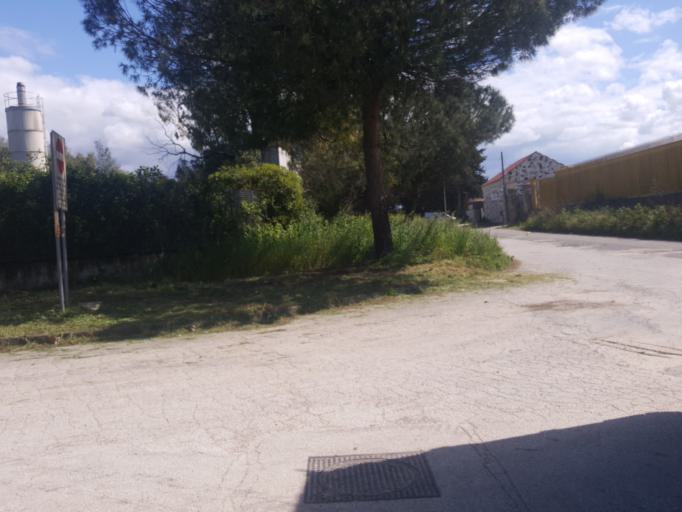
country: IT
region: Campania
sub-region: Provincia di Napoli
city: Torretta-Scalzapecora
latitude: 40.9340
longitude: 14.1056
